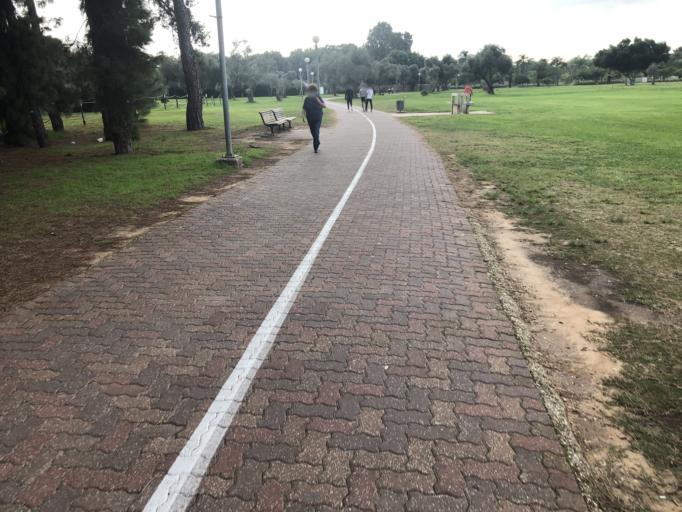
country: IL
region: Tel Aviv
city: Giv`atayim
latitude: 32.0483
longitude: 34.8258
